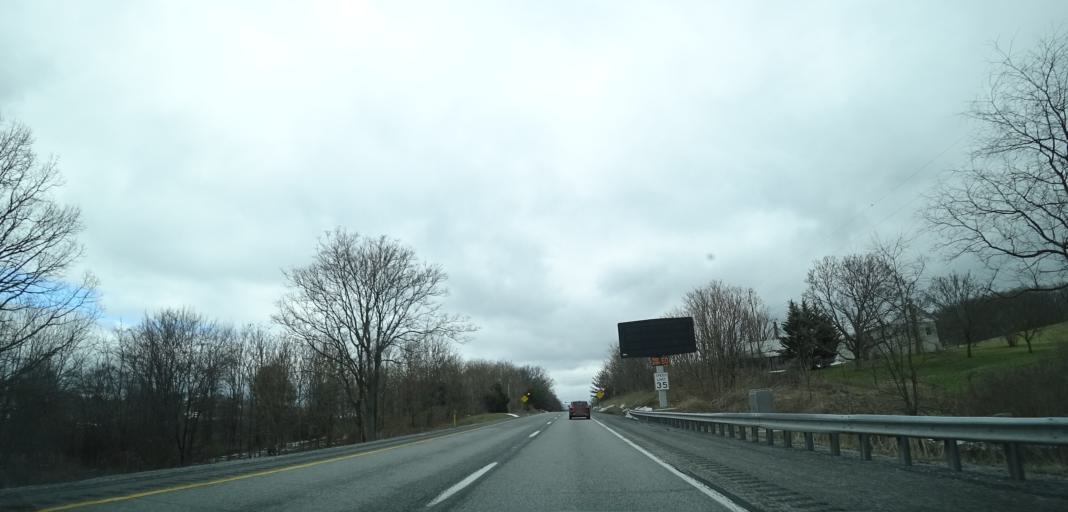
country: US
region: Pennsylvania
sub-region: Bedford County
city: Earlston
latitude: 39.9932
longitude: -78.2405
